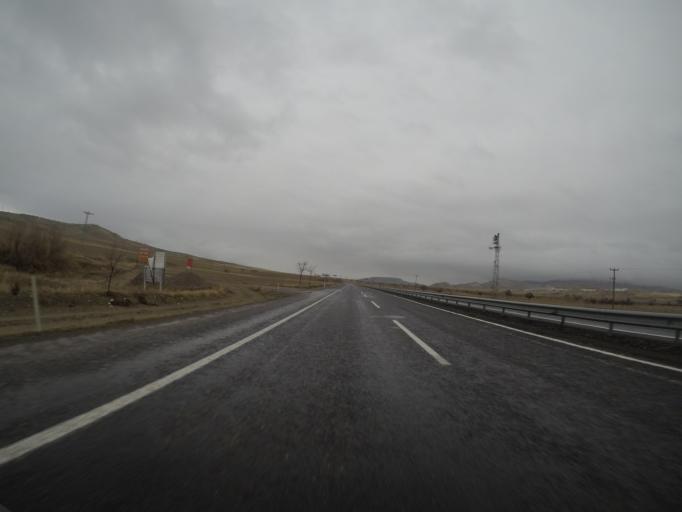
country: TR
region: Nevsehir
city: Avanos
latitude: 38.7125
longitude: 34.9208
